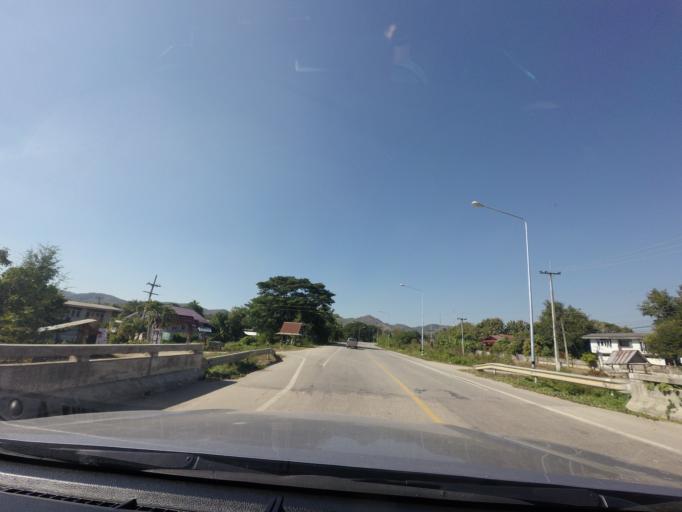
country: TH
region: Lampang
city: Chae Hom
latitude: 18.5108
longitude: 99.6447
